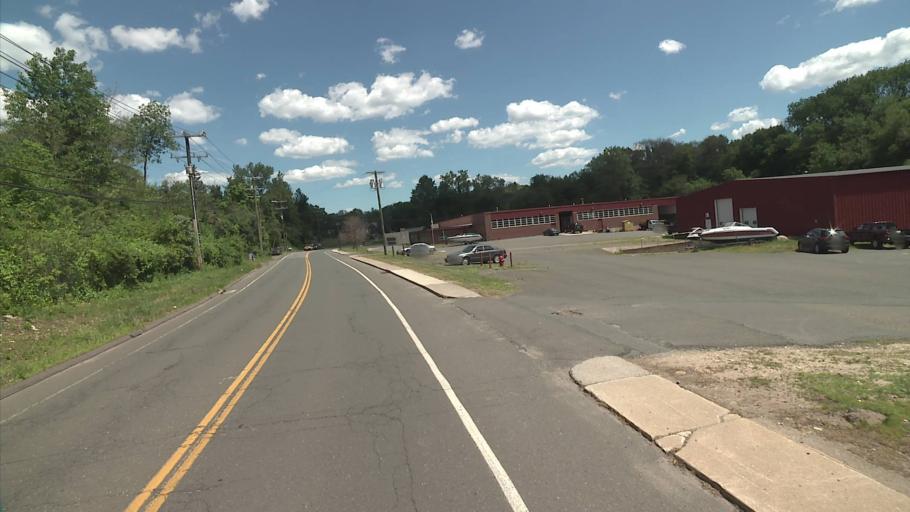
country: US
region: Connecticut
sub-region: Middlesex County
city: East Hampton
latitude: 41.5719
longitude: -72.5036
